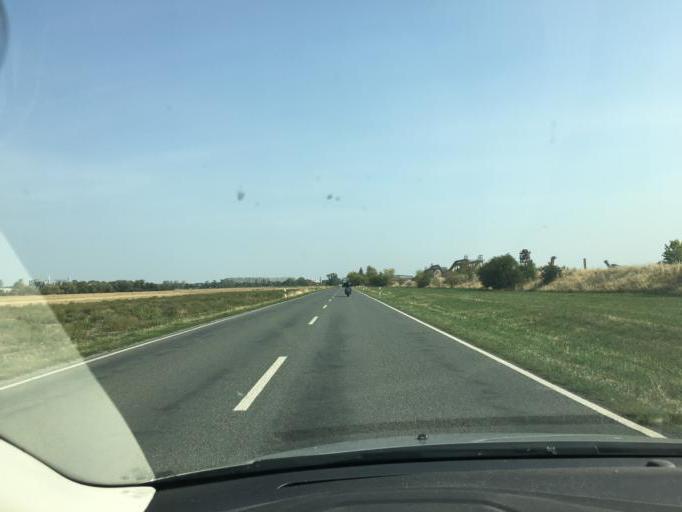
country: DE
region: Saxony-Anhalt
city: Barby
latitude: 51.9863
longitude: 11.8521
